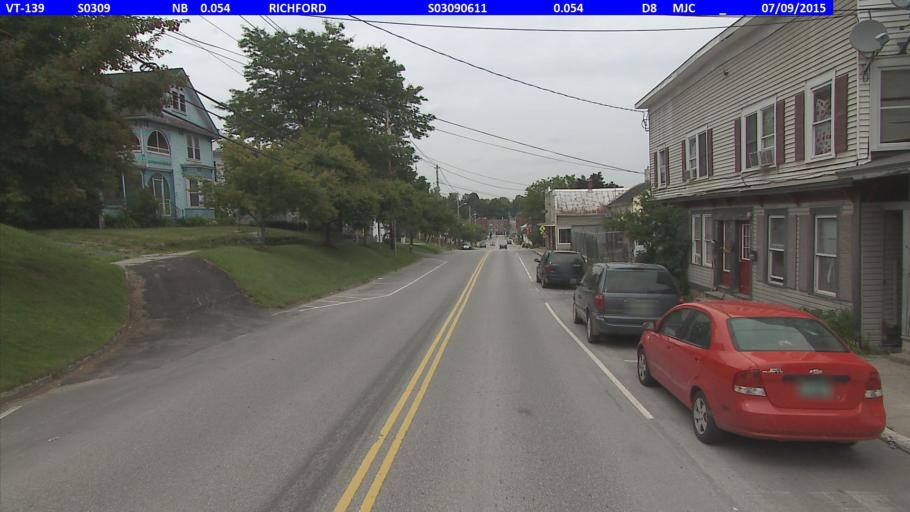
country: US
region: Vermont
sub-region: Franklin County
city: Richford
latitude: 44.9939
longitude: -72.6736
